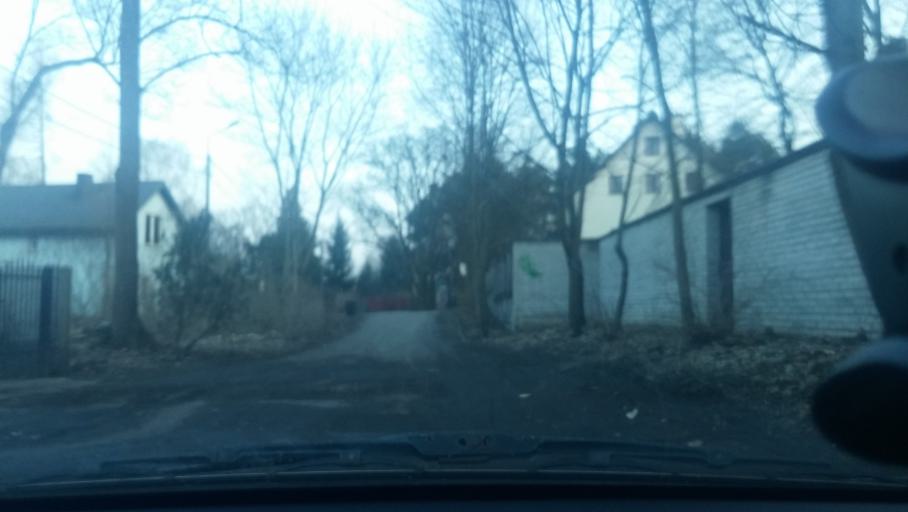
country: PL
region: Masovian Voivodeship
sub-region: Warszawa
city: Wawer
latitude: 52.1481
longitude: 21.1788
